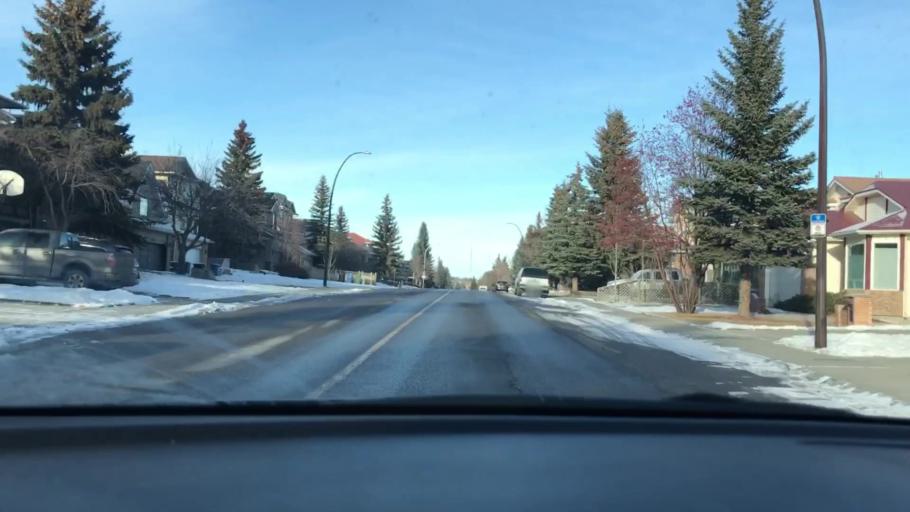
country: CA
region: Alberta
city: Calgary
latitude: 51.0255
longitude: -114.1702
